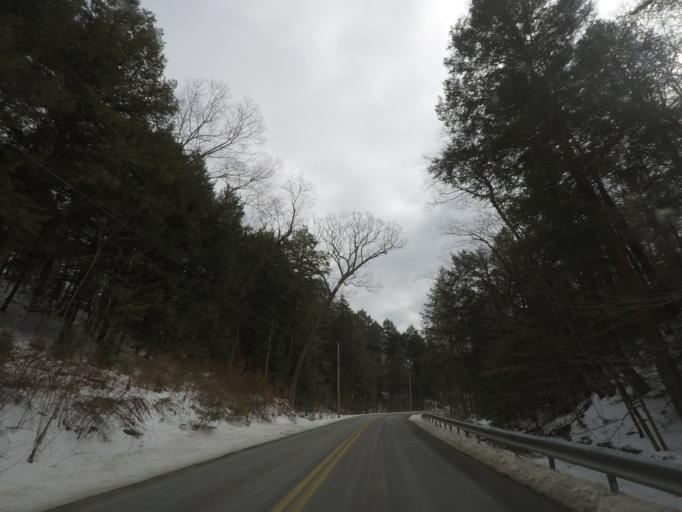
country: US
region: New York
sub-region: Rensselaer County
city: Hoosick Falls
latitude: 42.8803
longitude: -73.4136
